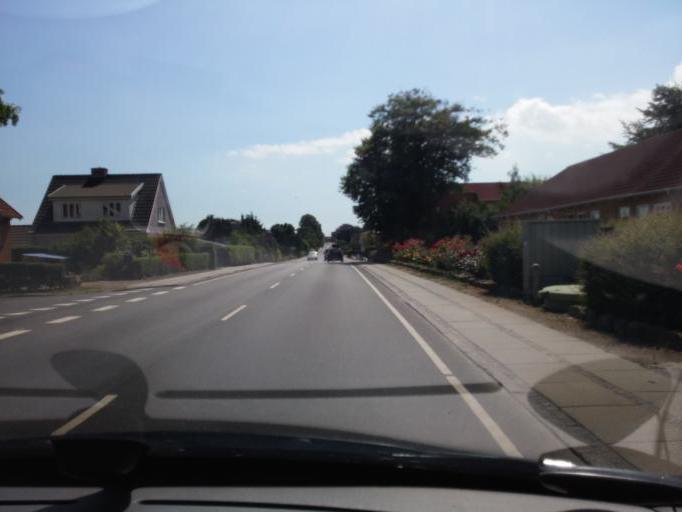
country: DK
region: South Denmark
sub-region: Langeland Kommune
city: Rudkobing
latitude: 54.8325
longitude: 10.7019
